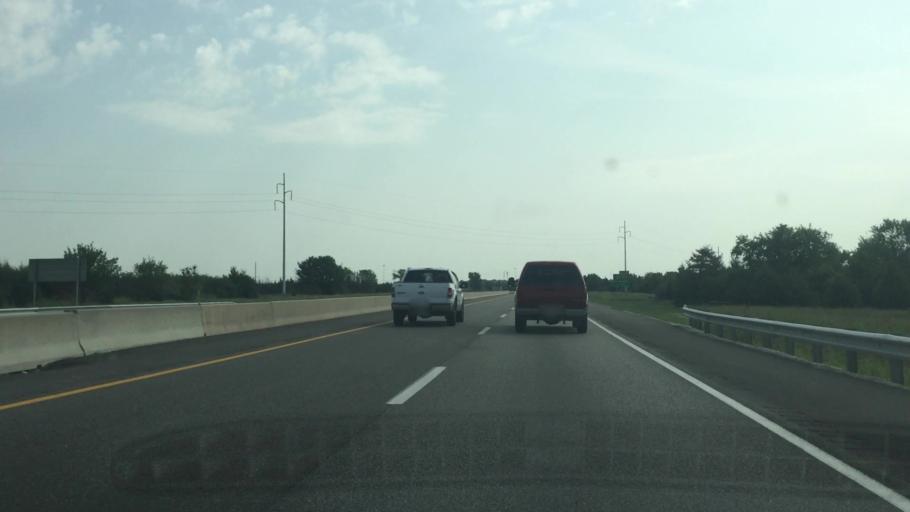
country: US
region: Kansas
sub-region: Butler County
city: El Dorado
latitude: 37.8125
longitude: -96.9127
